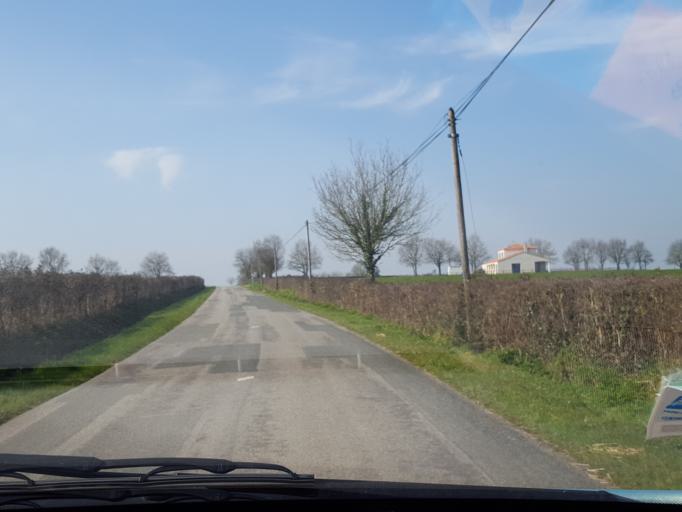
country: FR
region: Pays de la Loire
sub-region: Departement de la Vendee
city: Vendrennes
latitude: 46.8249
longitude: -1.1323
